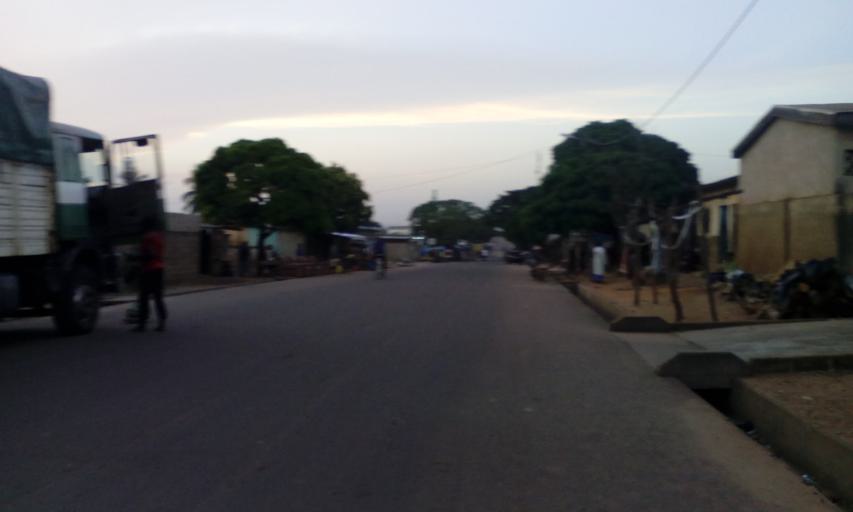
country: CI
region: Zanzan
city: Bondoukou
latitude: 8.0393
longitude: -2.7972
